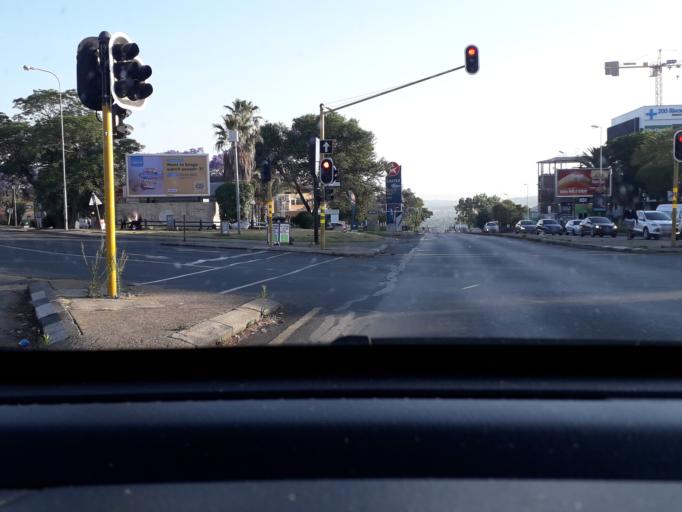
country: ZA
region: Gauteng
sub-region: City of Johannesburg Metropolitan Municipality
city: Modderfontein
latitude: -26.0811
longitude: 28.0620
